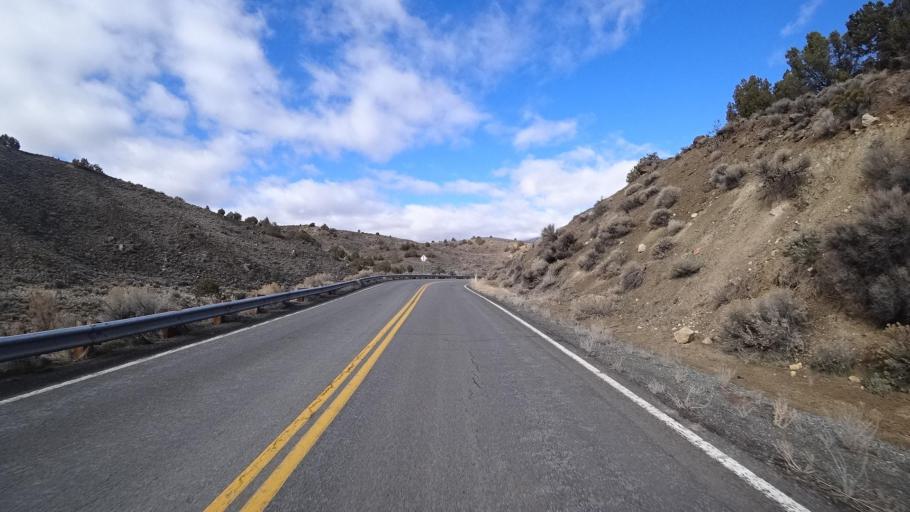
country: US
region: Nevada
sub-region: Washoe County
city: Cold Springs
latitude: 39.9028
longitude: -119.9965
